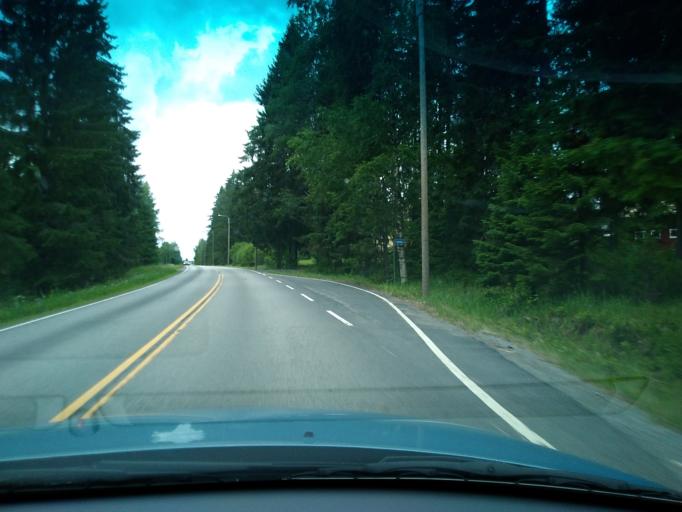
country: FI
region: Central Finland
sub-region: Saarijaervi-Viitasaari
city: Pylkoenmaeki
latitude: 62.6470
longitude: 24.9373
